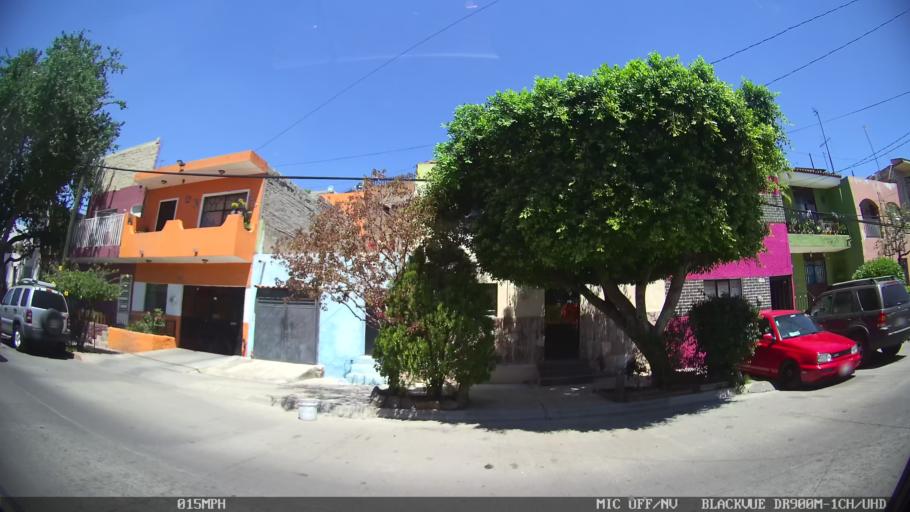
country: MX
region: Jalisco
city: Tlaquepaque
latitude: 20.6845
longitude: -103.2914
